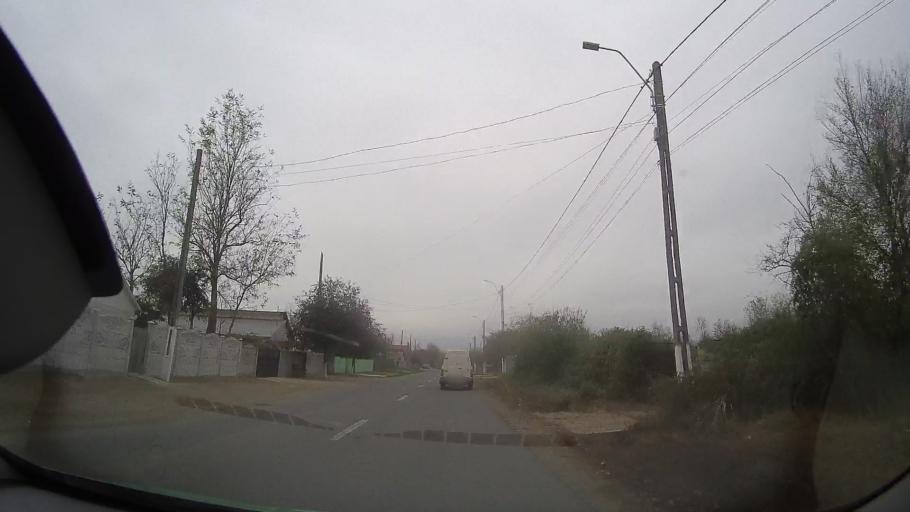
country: RO
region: Braila
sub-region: Comuna Budesti
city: Tataru
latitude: 44.8528
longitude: 27.4229
